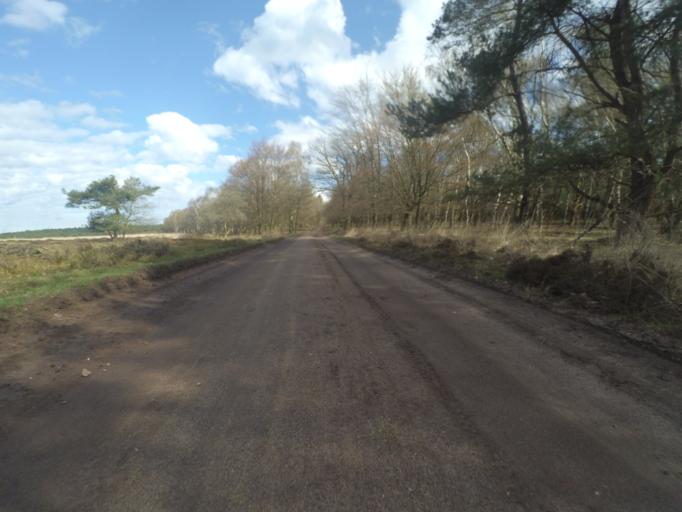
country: NL
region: Gelderland
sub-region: Gemeente Rozendaal
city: Rozendaal
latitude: 52.0786
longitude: 5.9422
